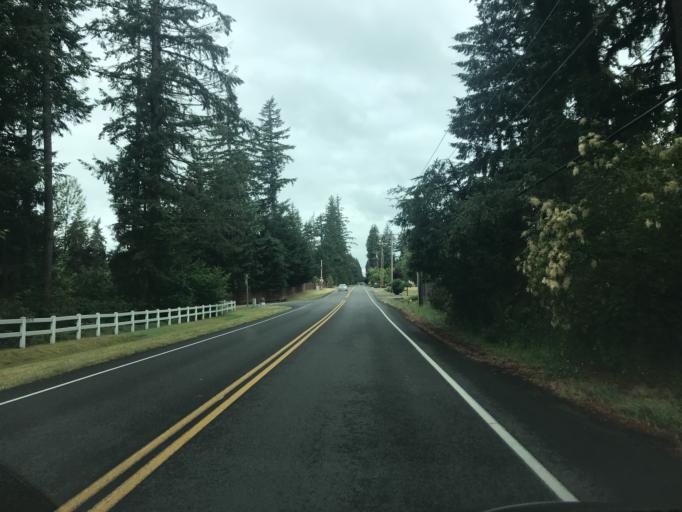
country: US
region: Washington
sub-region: King County
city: Black Diamond
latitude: 47.3435
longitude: -122.0314
